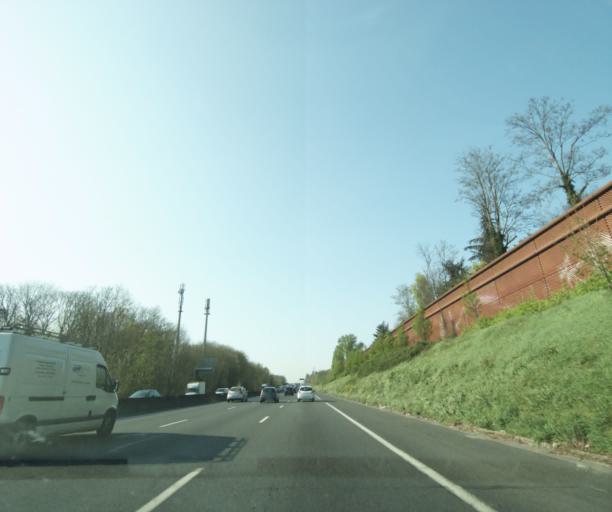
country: FR
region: Ile-de-France
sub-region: Departement de l'Essonne
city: Villemoisson-sur-Orge
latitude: 48.6837
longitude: 2.3289
